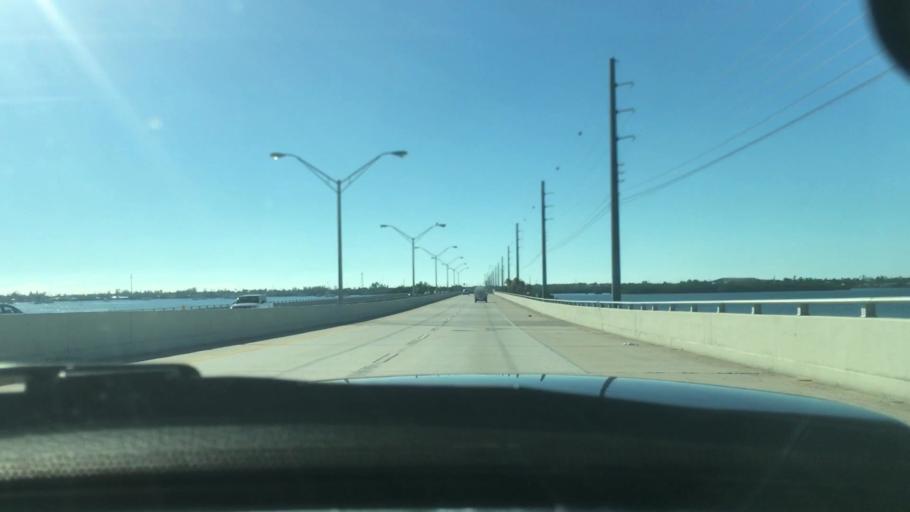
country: US
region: Florida
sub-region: Monroe County
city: Stock Island
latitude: 24.5775
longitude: -81.7180
